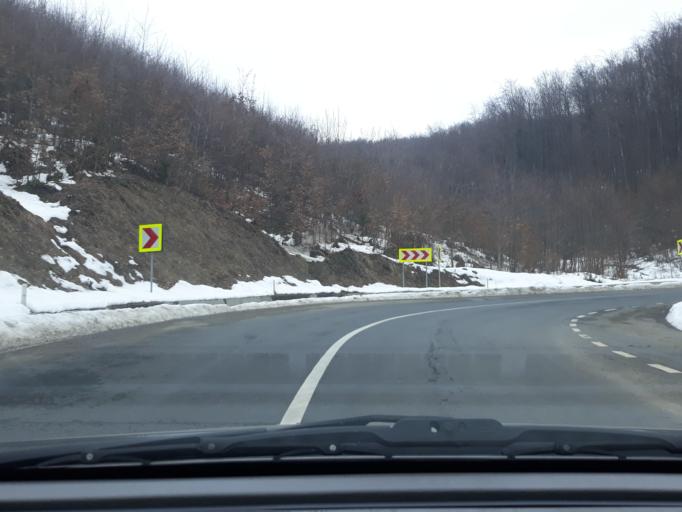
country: RO
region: Bihor
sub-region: Oras Alesd
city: Padurea Neagra
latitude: 47.1302
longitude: 22.4217
